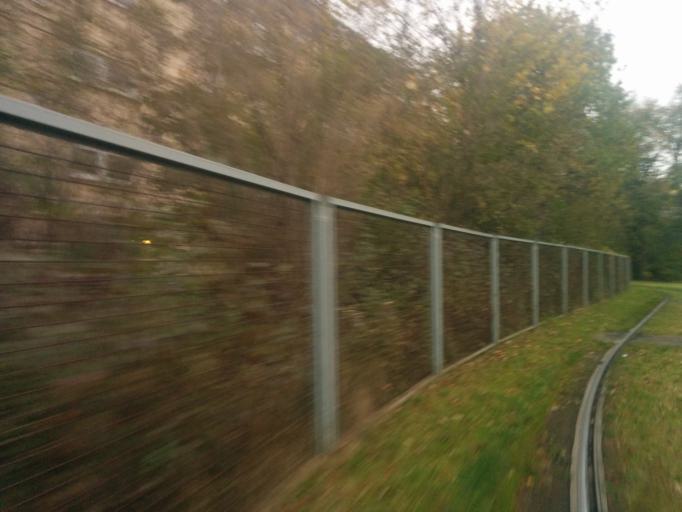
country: DE
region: Bavaria
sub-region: Upper Bavaria
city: Pasing
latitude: 48.1248
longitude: 11.4909
